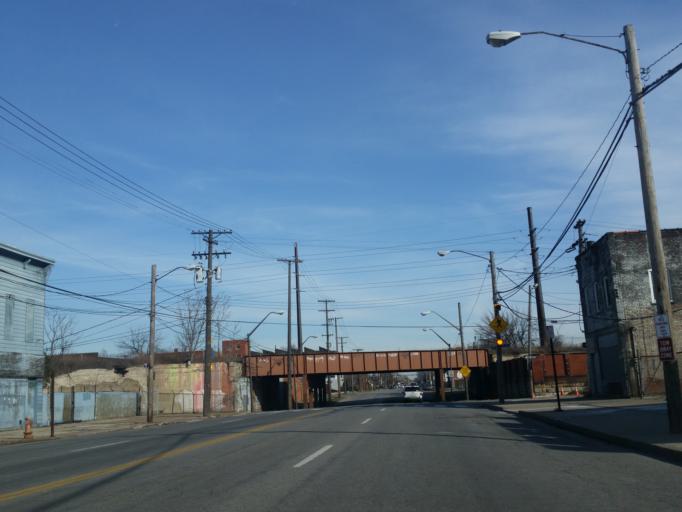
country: US
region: Ohio
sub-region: Cuyahoga County
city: Cleveland
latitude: 41.5145
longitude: -81.6683
